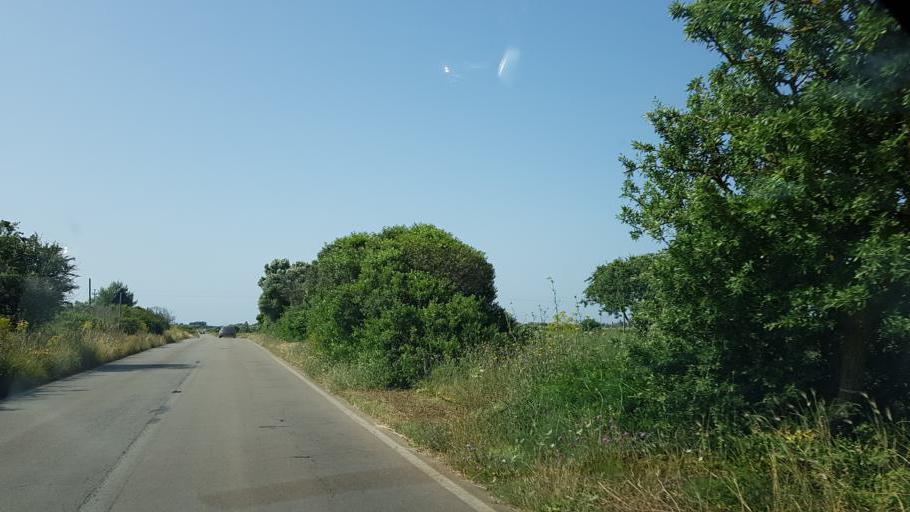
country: IT
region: Apulia
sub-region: Provincia di Brindisi
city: San Pancrazio Salentino
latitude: 40.3388
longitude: 17.8494
